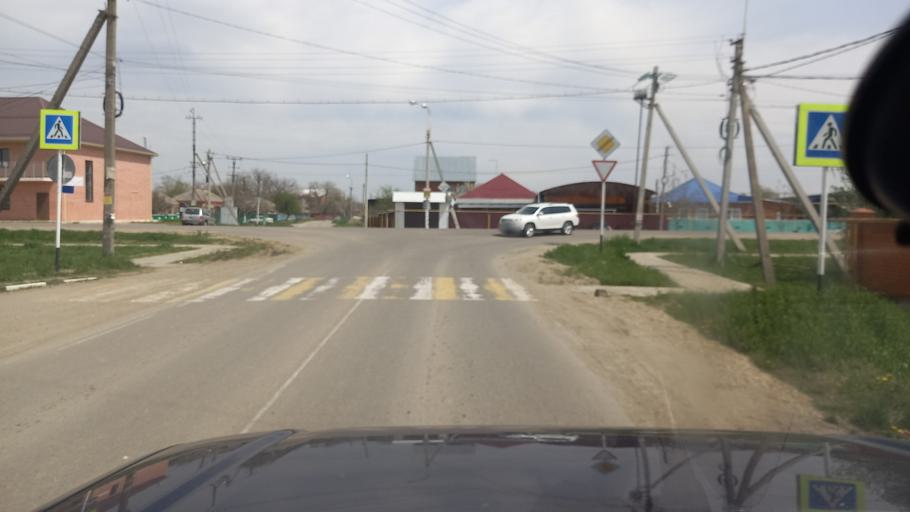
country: RU
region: Adygeya
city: Yablonovskiy
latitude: 44.9892
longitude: 38.9982
